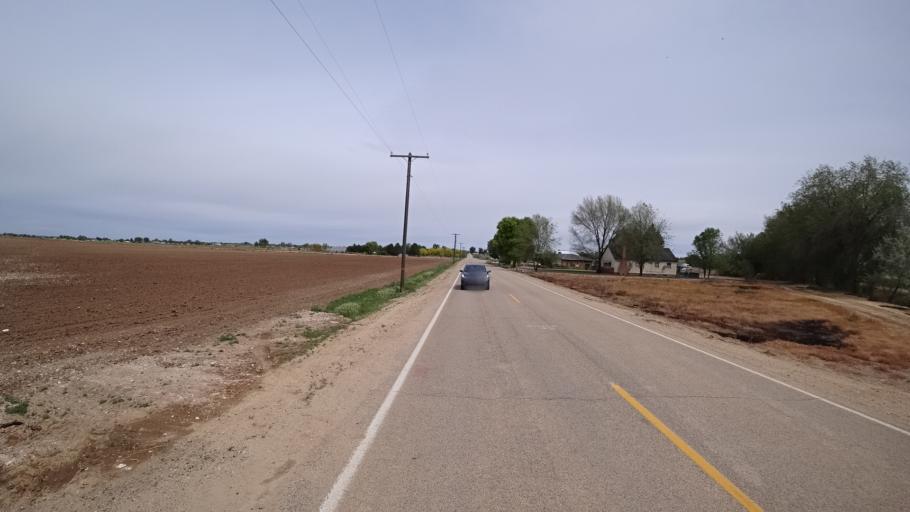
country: US
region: Idaho
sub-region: Ada County
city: Kuna
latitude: 43.5507
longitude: -116.4737
